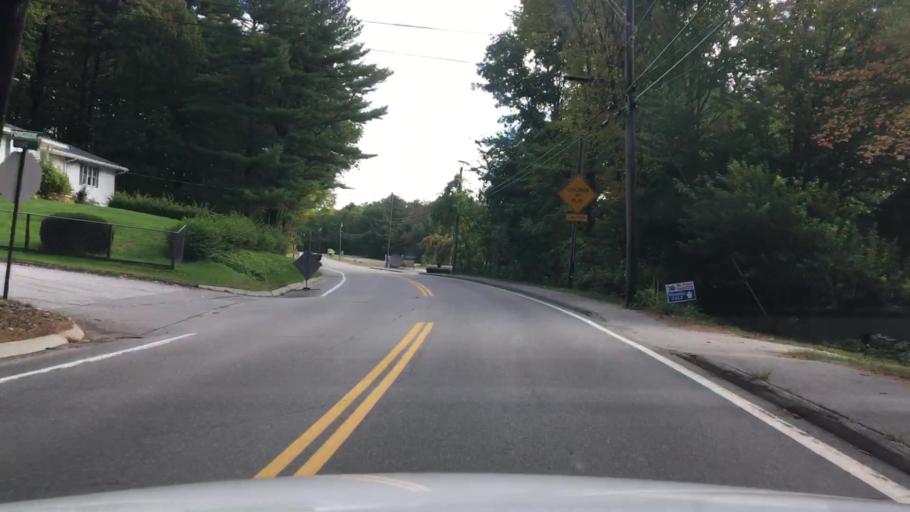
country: US
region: Maine
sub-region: Cumberland County
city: Brunswick
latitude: 43.9236
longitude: -69.9450
